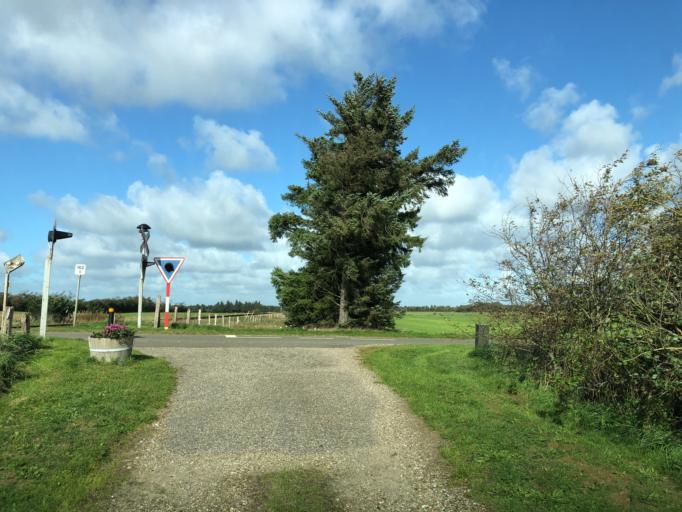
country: DK
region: Central Jutland
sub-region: Holstebro Kommune
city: Ulfborg
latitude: 56.2886
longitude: 8.3296
